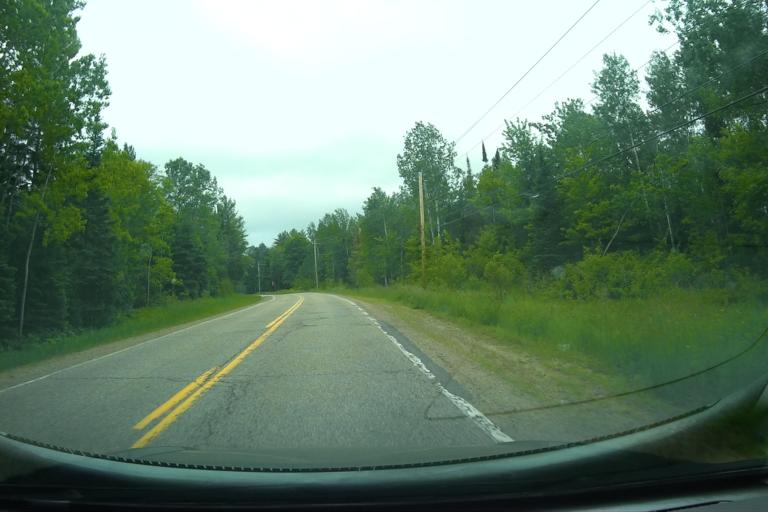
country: CA
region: Ontario
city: Pembroke
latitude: 45.4830
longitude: -77.2091
